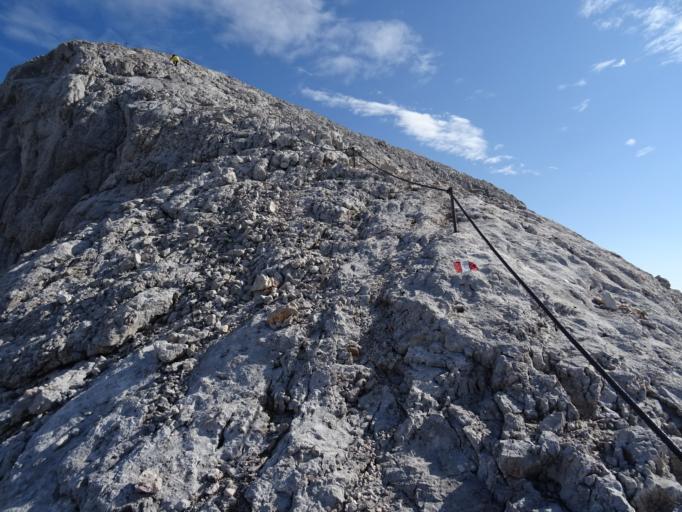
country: AT
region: Styria
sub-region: Politischer Bezirk Liezen
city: Schladming
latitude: 47.4806
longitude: 13.6318
